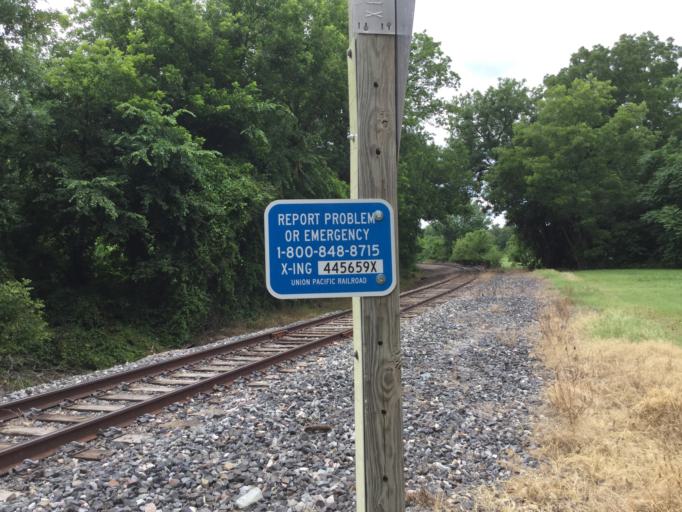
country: US
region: Kansas
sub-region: Montgomery County
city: Independence
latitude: 37.2148
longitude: -95.7068
